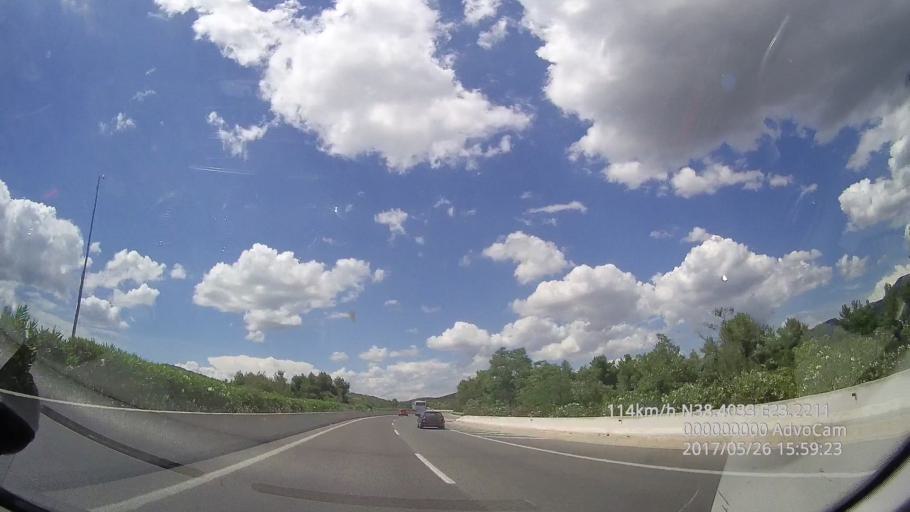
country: GR
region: Central Greece
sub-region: Nomos Fthiotidos
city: Ayios Konstandinos
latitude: 38.7651
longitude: 22.8385
